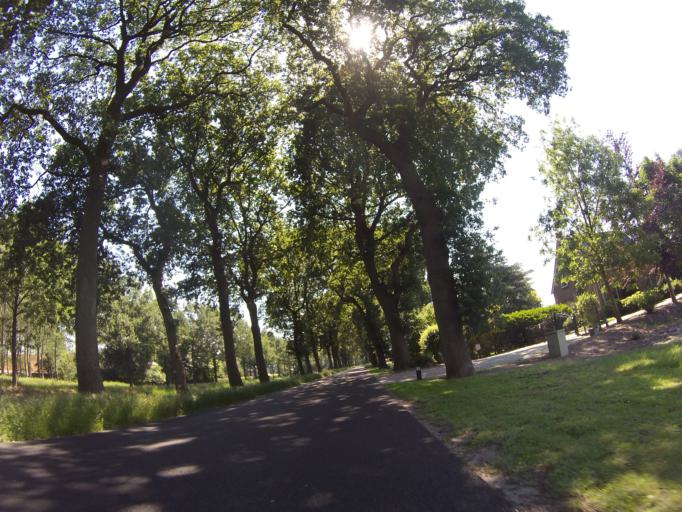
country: NL
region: Drenthe
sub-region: Gemeente Coevorden
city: Sleen
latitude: 52.8355
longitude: 6.8027
